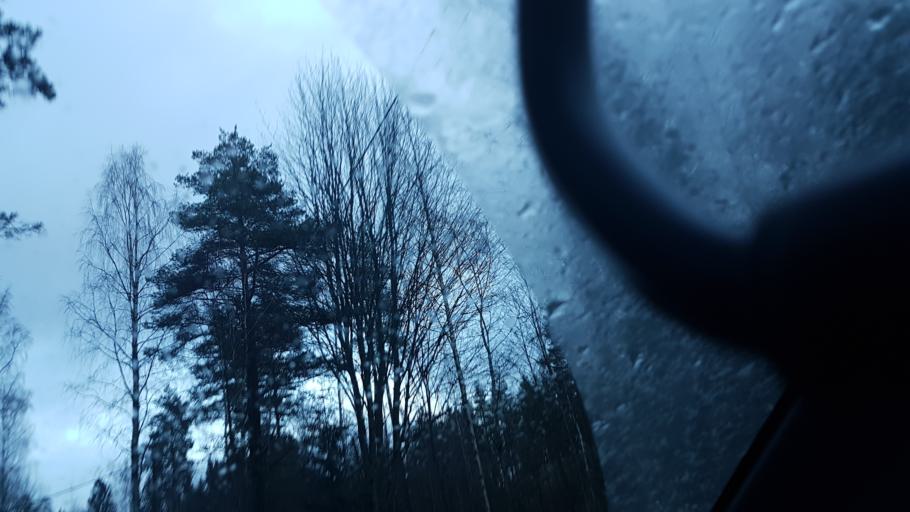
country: FI
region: Uusimaa
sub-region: Helsinki
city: Lohja
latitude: 60.2144
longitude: 24.0903
